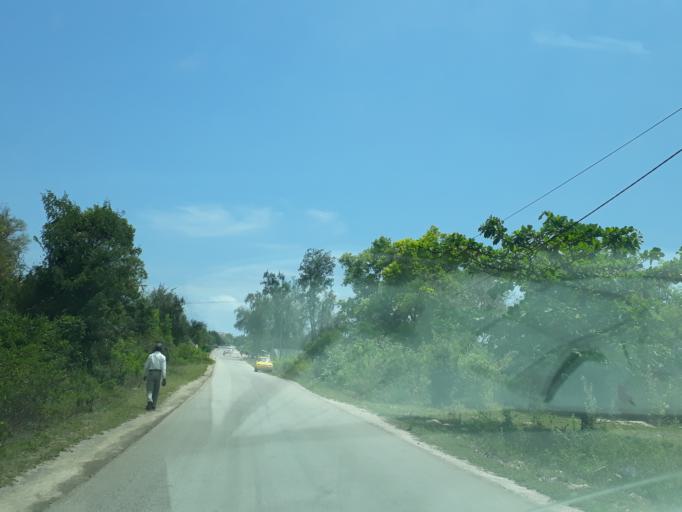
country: TZ
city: Kiwengwa
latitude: -5.9917
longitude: 39.3709
